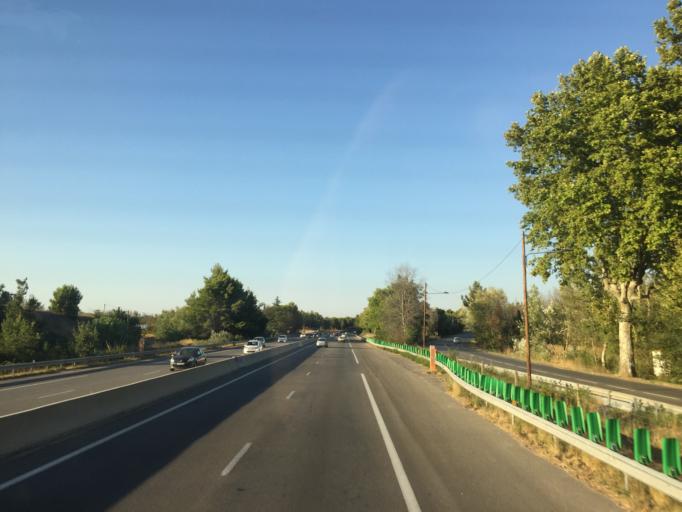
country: FR
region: Provence-Alpes-Cote d'Azur
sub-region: Departement des Bouches-du-Rhone
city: Venelles
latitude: 43.5679
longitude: 5.4655
